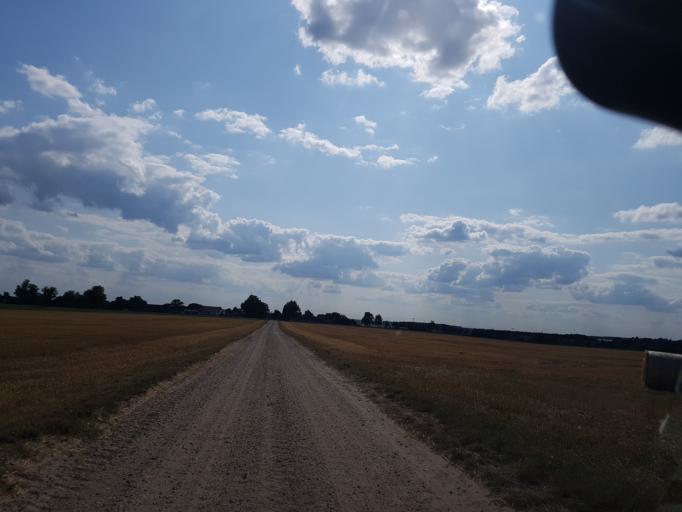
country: DE
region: Brandenburg
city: Finsterwalde
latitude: 51.6349
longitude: 13.7697
